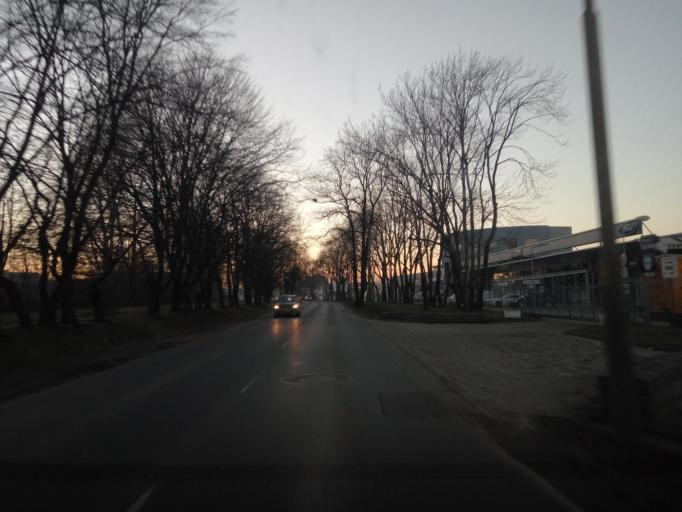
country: PL
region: Lower Silesian Voivodeship
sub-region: Powiat wroclawski
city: Wroclaw
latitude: 51.1142
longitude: 16.9760
